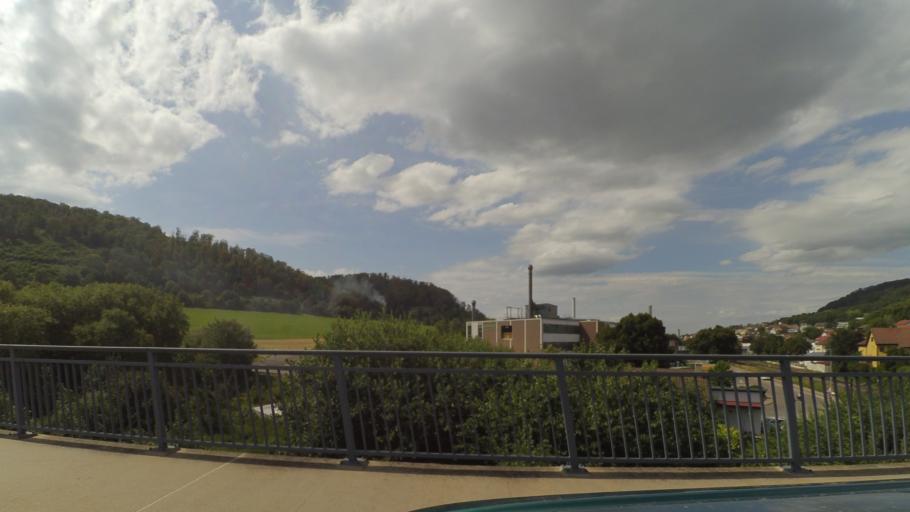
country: DE
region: Baden-Wuerttemberg
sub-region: Regierungsbezirk Stuttgart
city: Oberkochen
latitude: 48.8108
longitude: 10.1277
